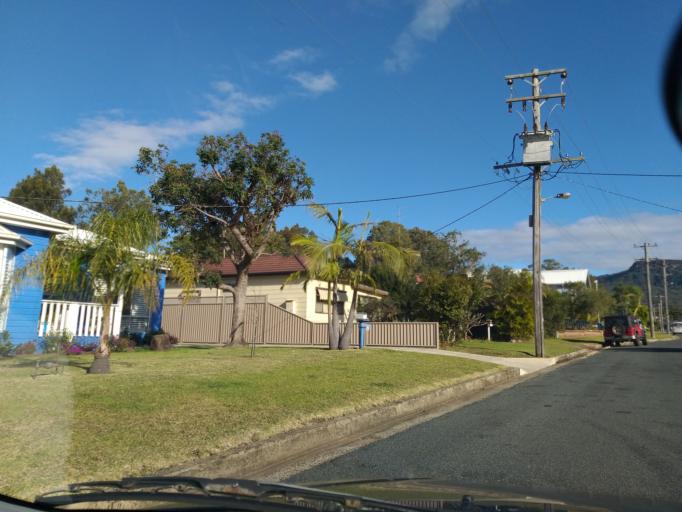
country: AU
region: New South Wales
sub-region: Wollongong
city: East Corrimal
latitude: -34.3722
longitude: 150.9130
